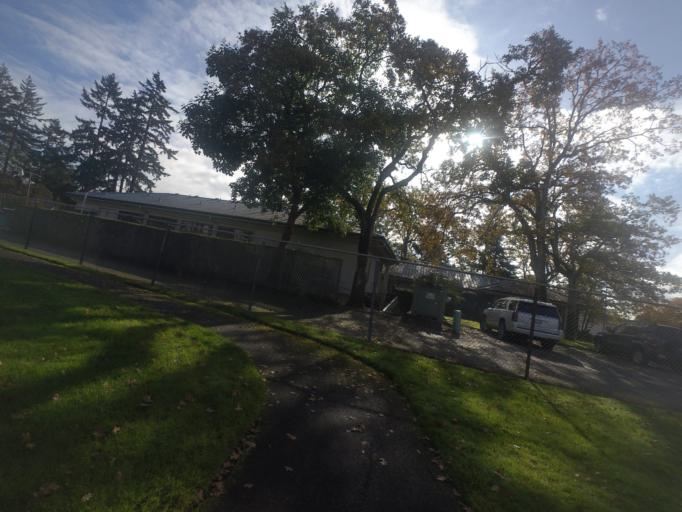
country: US
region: Washington
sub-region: Pierce County
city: Lakewood
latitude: 47.1750
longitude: -122.5175
